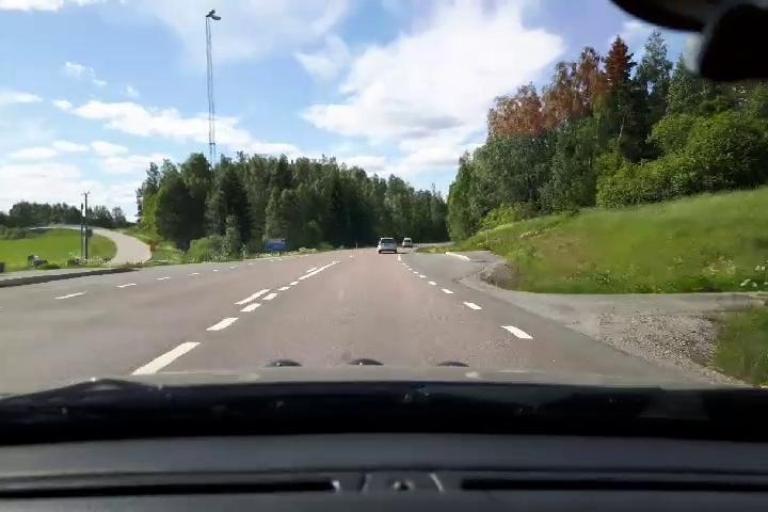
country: SE
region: Gaevleborg
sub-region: Bollnas Kommun
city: Bollnas
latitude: 61.3124
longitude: 16.4451
